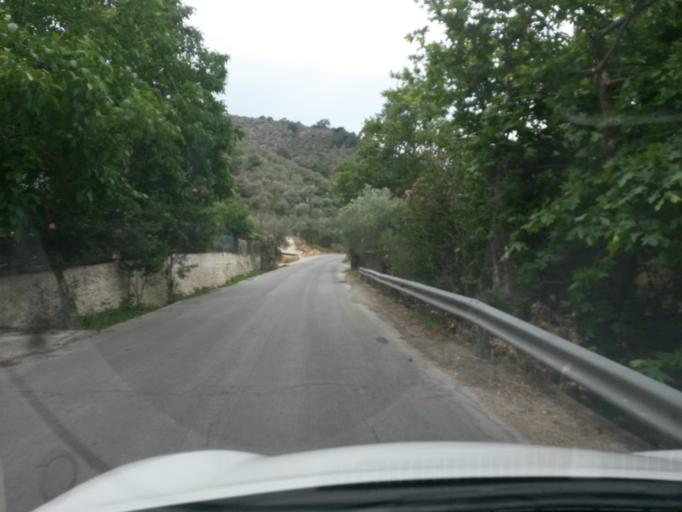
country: GR
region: North Aegean
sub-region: Nomos Lesvou
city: Skopelos
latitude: 38.9922
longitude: 26.4480
